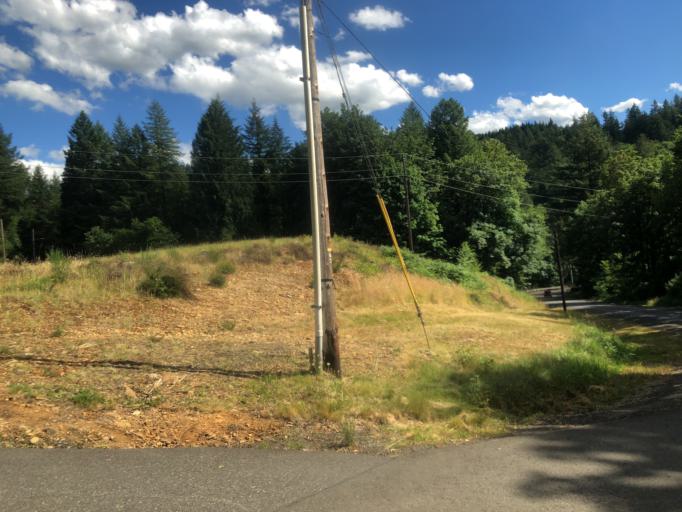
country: US
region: Oregon
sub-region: Clackamas County
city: Sandy
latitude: 45.4299
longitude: -122.2319
